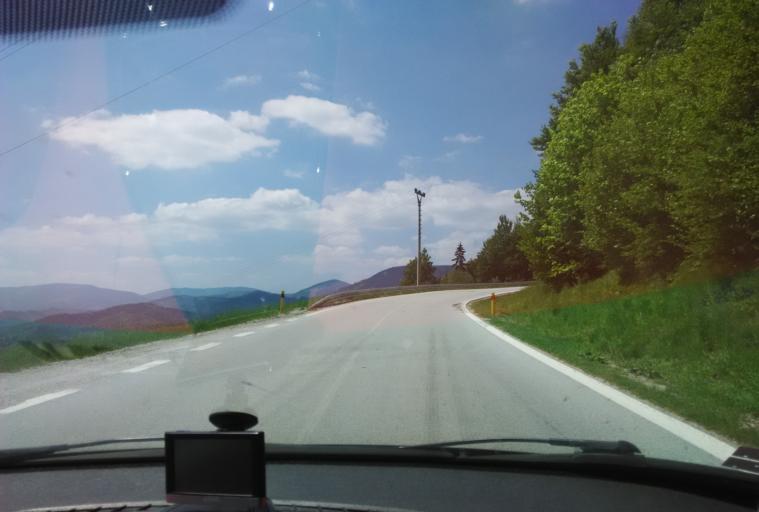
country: SK
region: Kosicky
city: Dobsina
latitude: 48.8460
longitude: 20.3810
